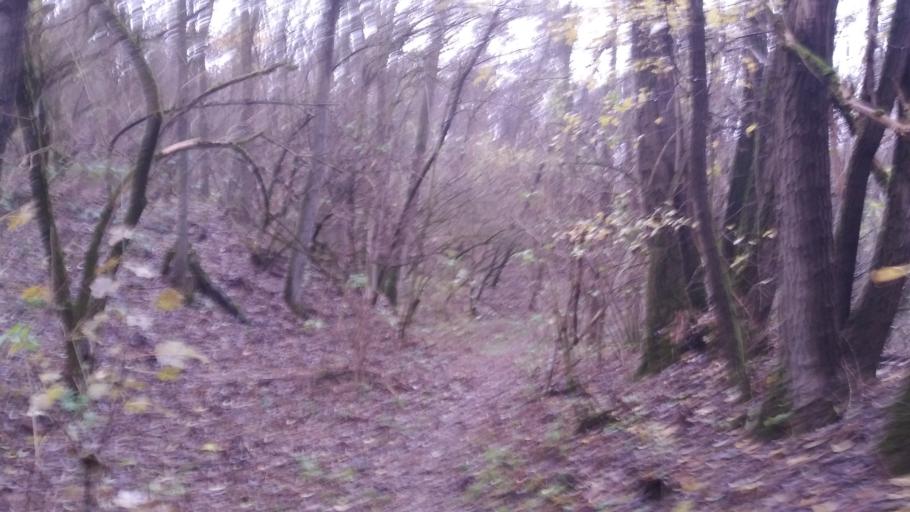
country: HU
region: Pest
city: Pilisszentivan
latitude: 47.6027
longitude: 18.9062
